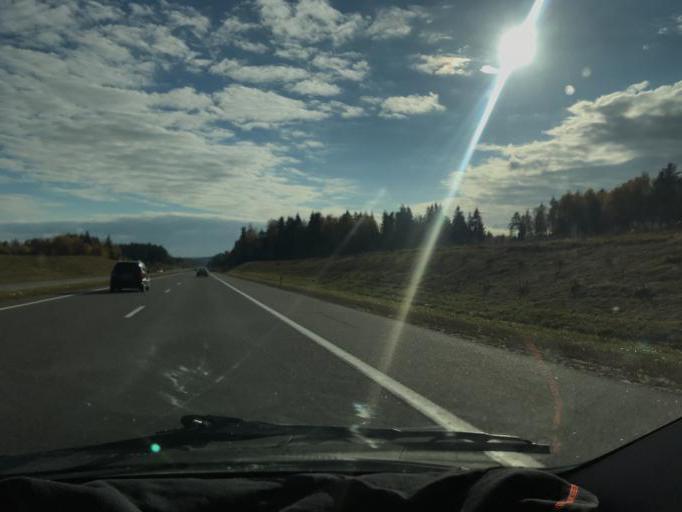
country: BY
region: Minsk
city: Lahoysk
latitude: 54.1428
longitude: 27.8093
